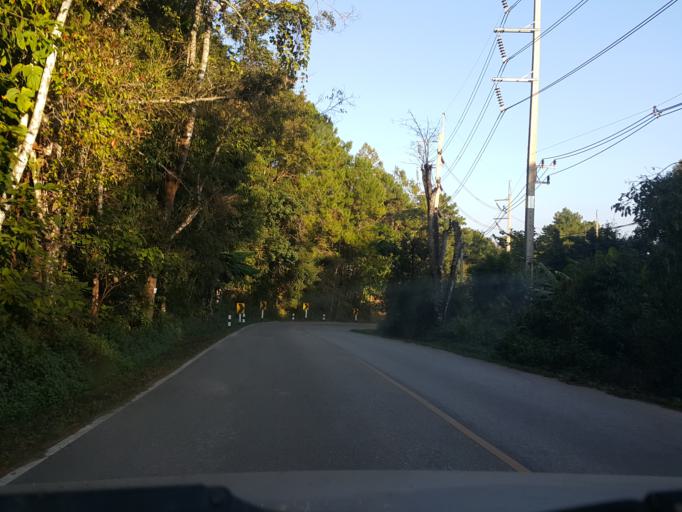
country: TH
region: Mae Hong Son
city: Mae Hi
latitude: 19.2786
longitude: 98.6143
